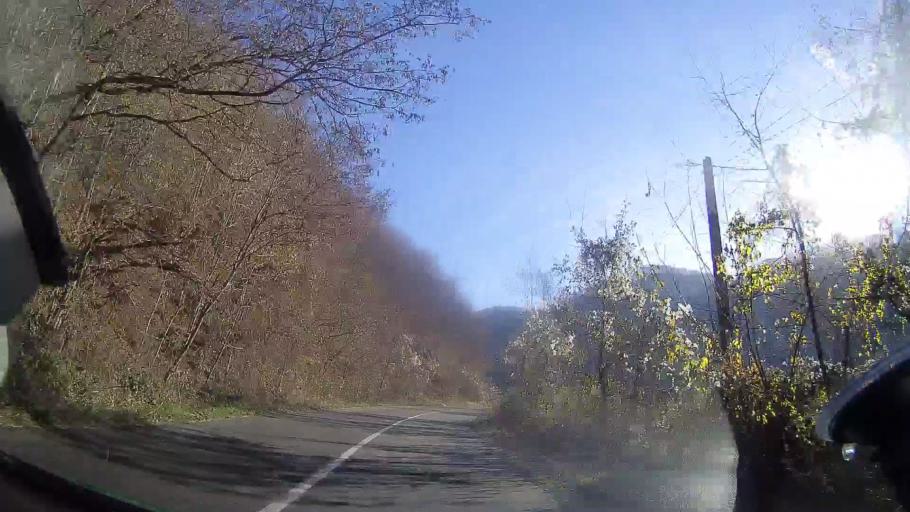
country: RO
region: Bihor
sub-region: Comuna Bulz
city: Bulz
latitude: 46.9168
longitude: 22.6565
